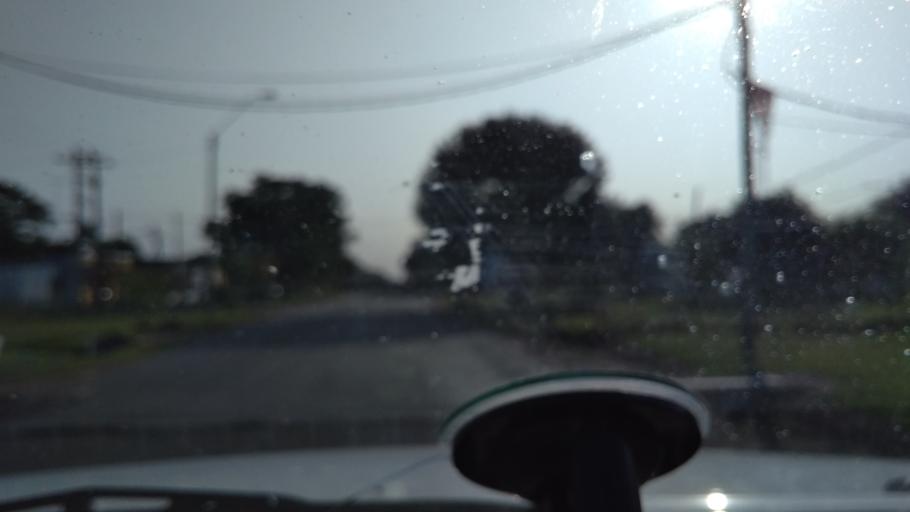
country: UY
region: Canelones
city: Santa Rosa
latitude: -34.4943
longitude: -56.0306
